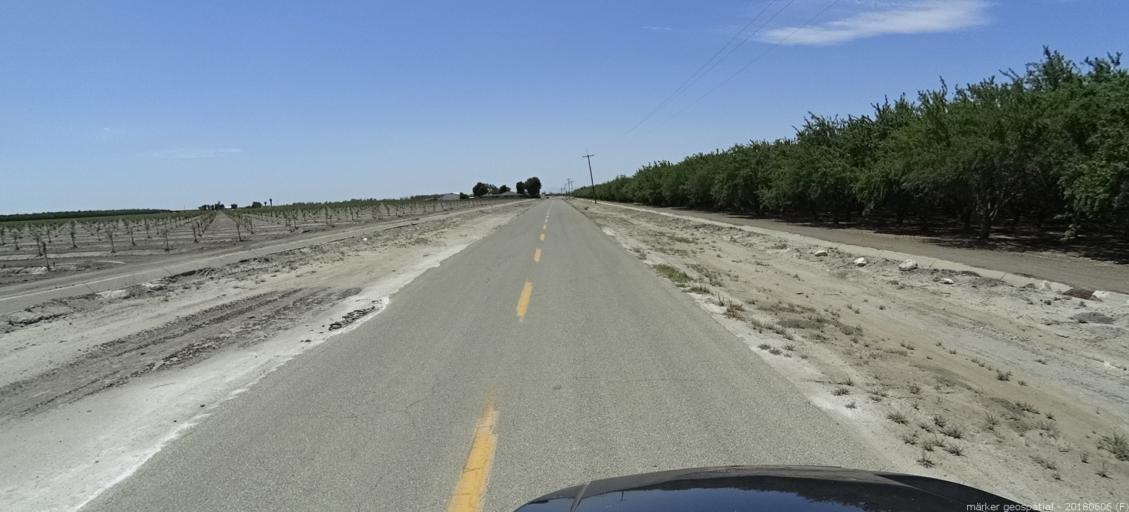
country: US
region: California
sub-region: Fresno County
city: Firebaugh
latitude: 36.8445
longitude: -120.3911
